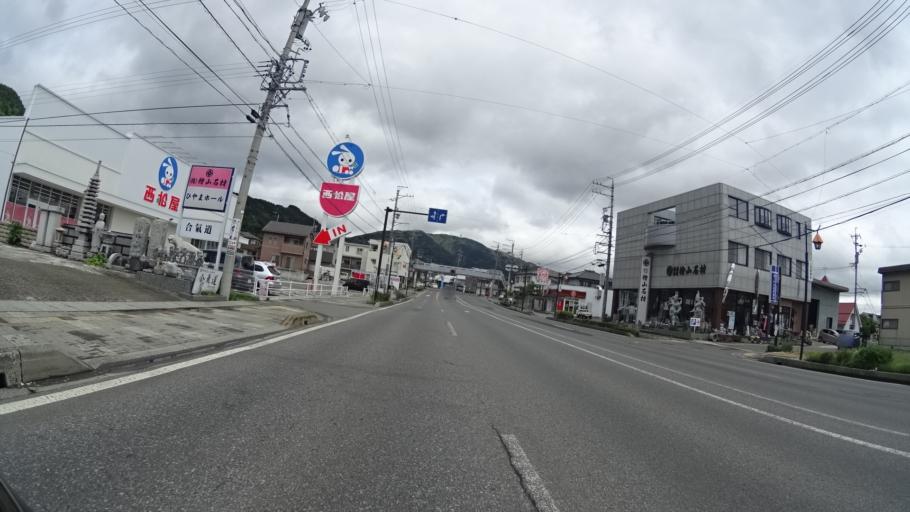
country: JP
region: Nagano
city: Nagano-shi
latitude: 36.6747
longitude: 138.1995
